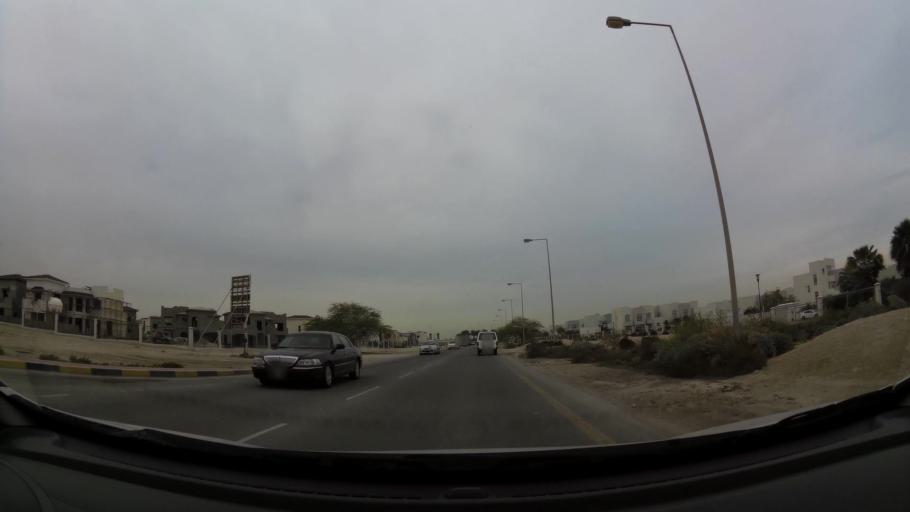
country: BH
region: Northern
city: Ar Rifa'
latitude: 26.0929
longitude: 50.5609
